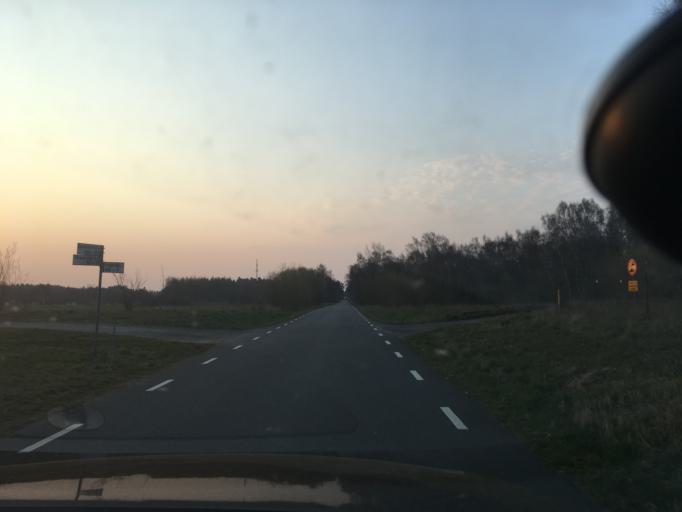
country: SE
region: Skane
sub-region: Simrishamns Kommun
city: Simrishamn
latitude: 55.3986
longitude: 14.1691
